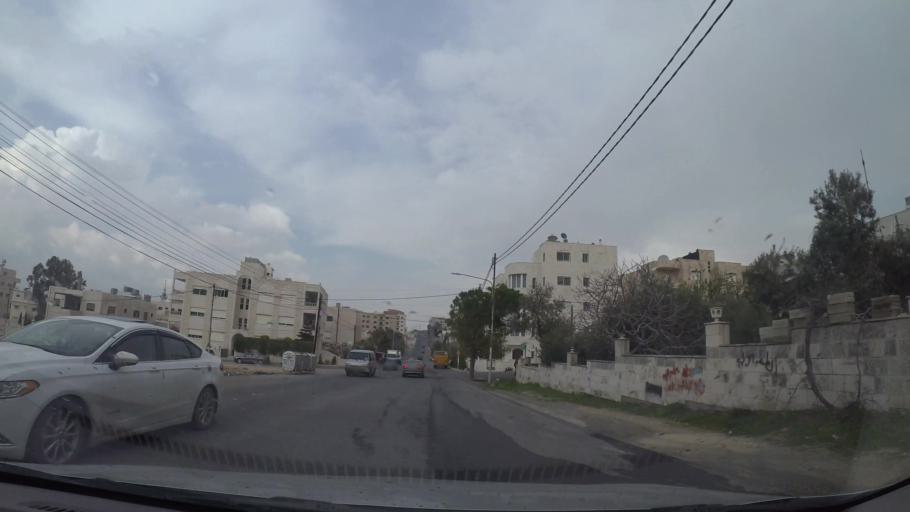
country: JO
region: Amman
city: Umm as Summaq
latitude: 31.8905
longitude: 35.8522
